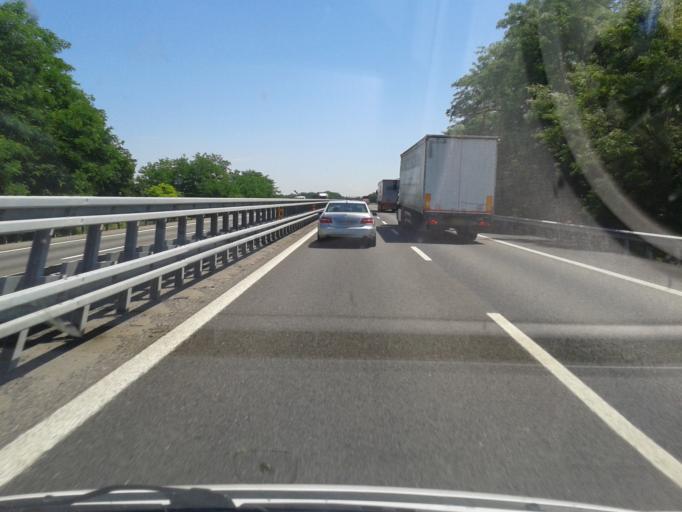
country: IT
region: Lombardy
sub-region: Provincia di Pavia
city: Portalbera
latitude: 45.0837
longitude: 9.3348
